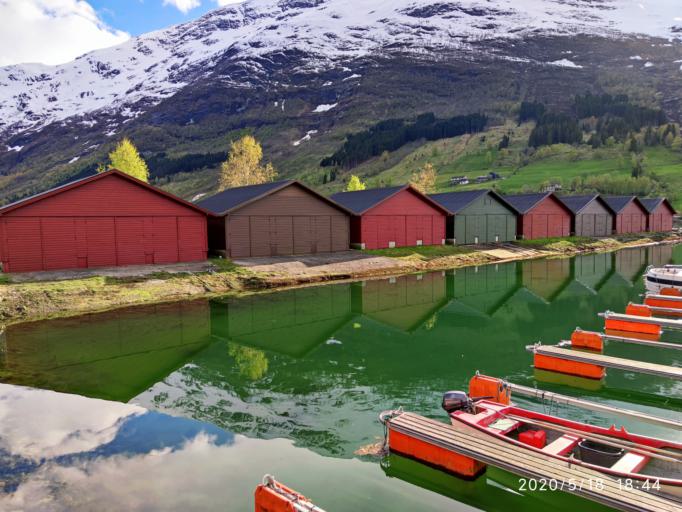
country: NO
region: Sogn og Fjordane
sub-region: Stryn
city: Stryn
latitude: 61.8394
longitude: 6.8103
